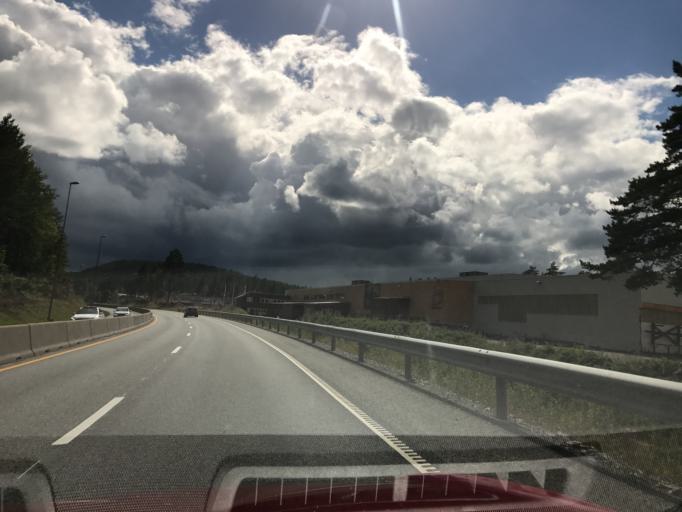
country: NO
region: Aust-Agder
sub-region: Gjerstad
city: Gjerstad
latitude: 58.8264
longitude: 9.0783
